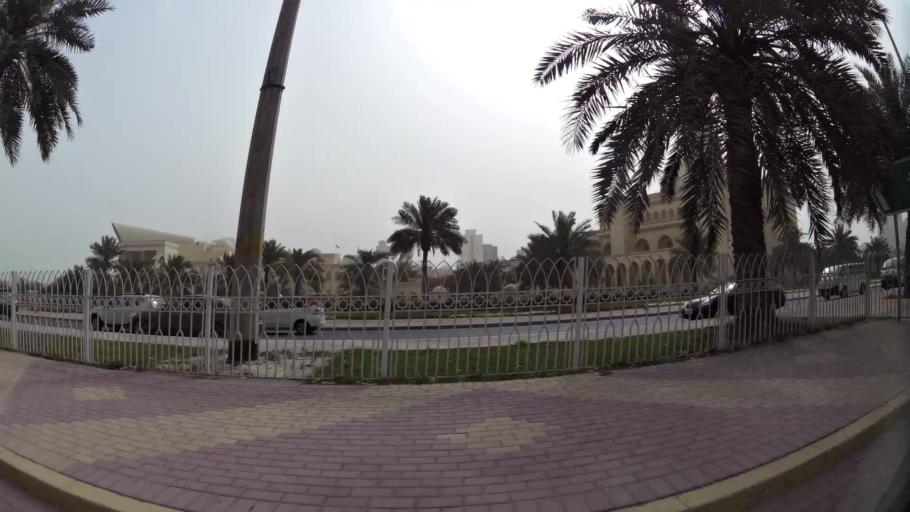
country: BH
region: Manama
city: Manama
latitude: 26.2198
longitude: 50.5971
